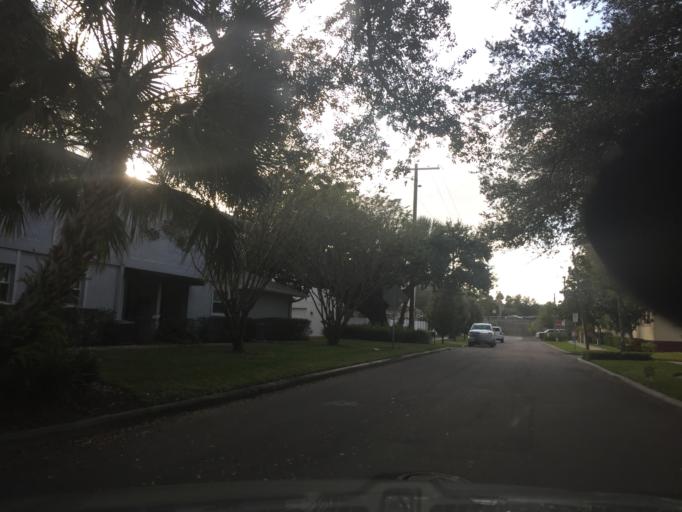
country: US
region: Florida
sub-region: Hillsborough County
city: Tampa
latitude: 27.9398
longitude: -82.4749
